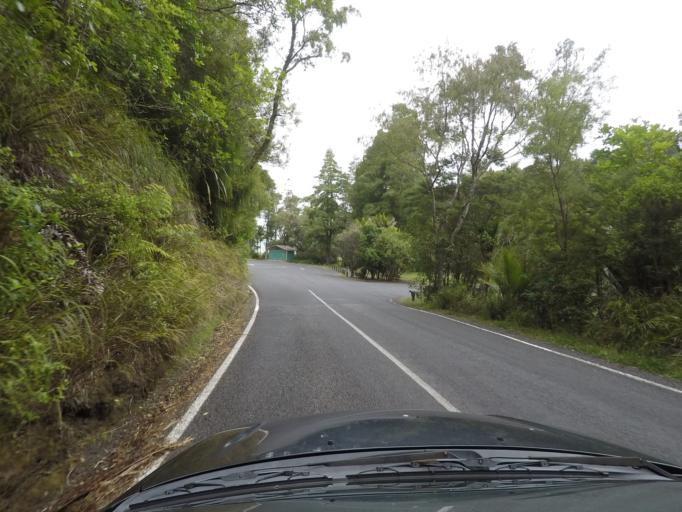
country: NZ
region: Auckland
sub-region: Auckland
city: Titirangi
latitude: -36.9497
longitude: 174.6584
